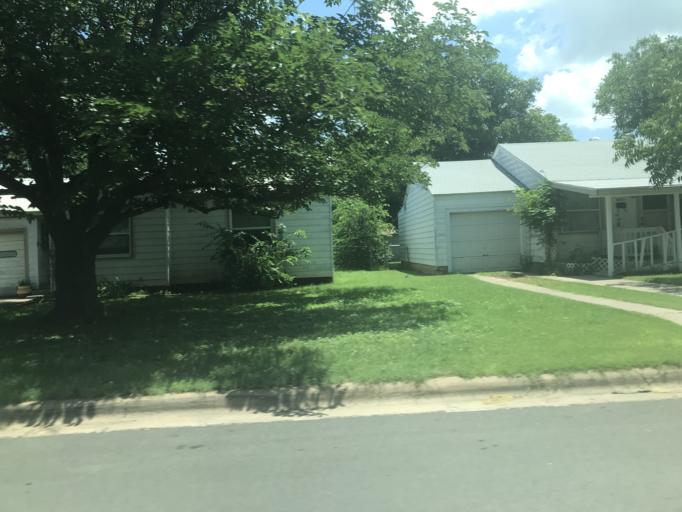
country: US
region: Texas
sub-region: Taylor County
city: Abilene
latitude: 32.4675
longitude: -99.7556
